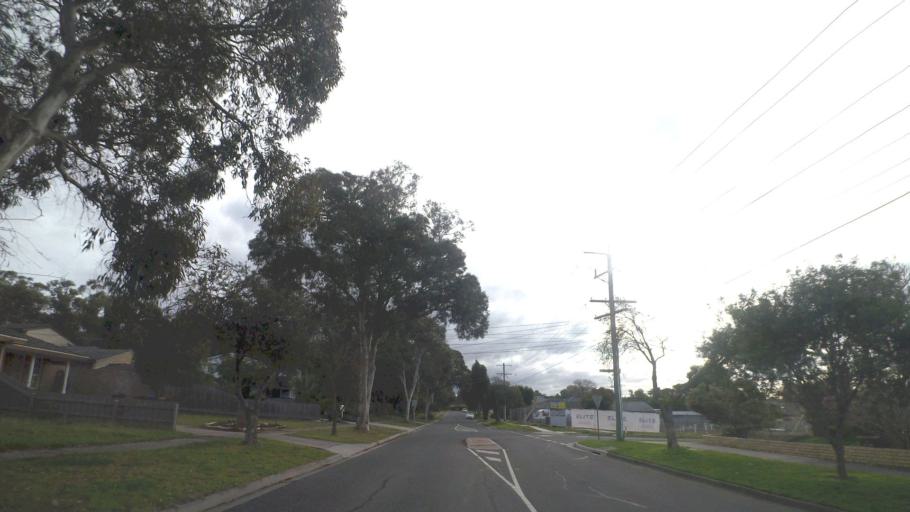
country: AU
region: Victoria
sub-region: Knox
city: Wantirna
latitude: -37.8422
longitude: 145.2228
